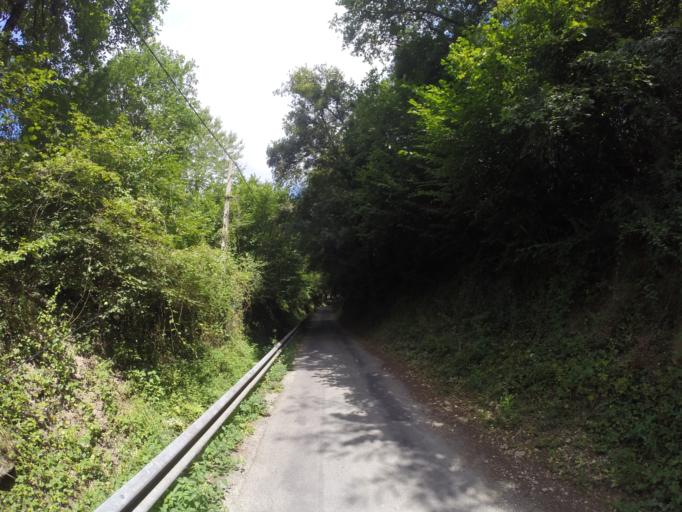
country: FR
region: Centre
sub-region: Departement d'Indre-et-Loire
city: Rochecorbon
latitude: 47.4128
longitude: 0.7171
